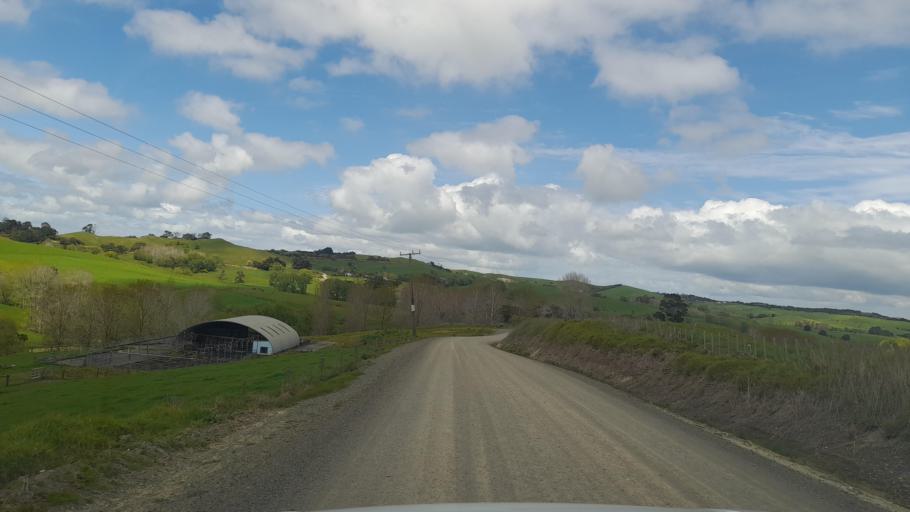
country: NZ
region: Auckland
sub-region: Auckland
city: Wellsford
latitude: -36.1709
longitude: 174.3187
